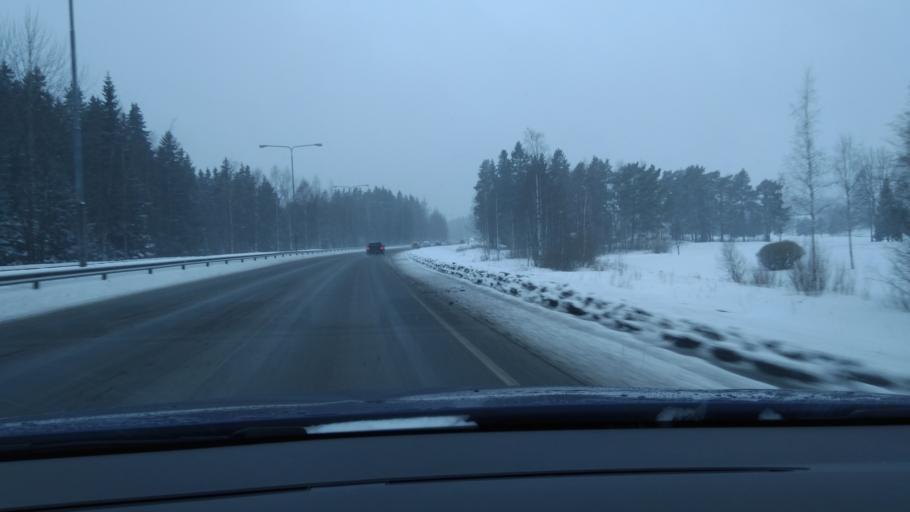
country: FI
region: Pirkanmaa
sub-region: Tampere
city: Tampere
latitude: 61.5037
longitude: 23.8571
